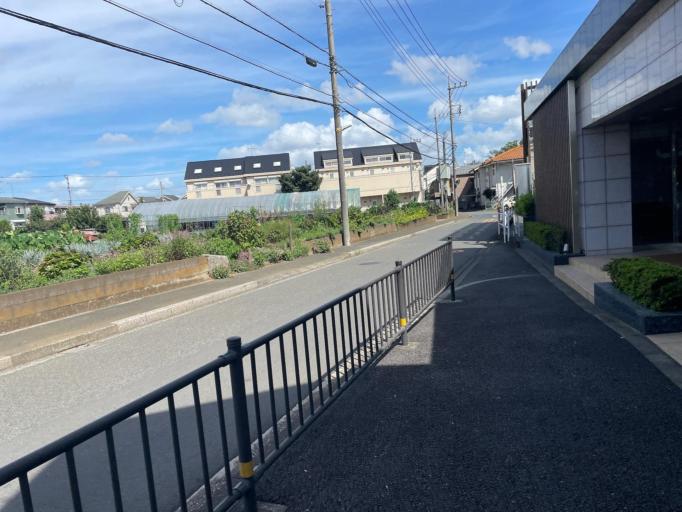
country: JP
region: Tokyo
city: Tanashicho
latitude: 35.7546
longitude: 139.5256
